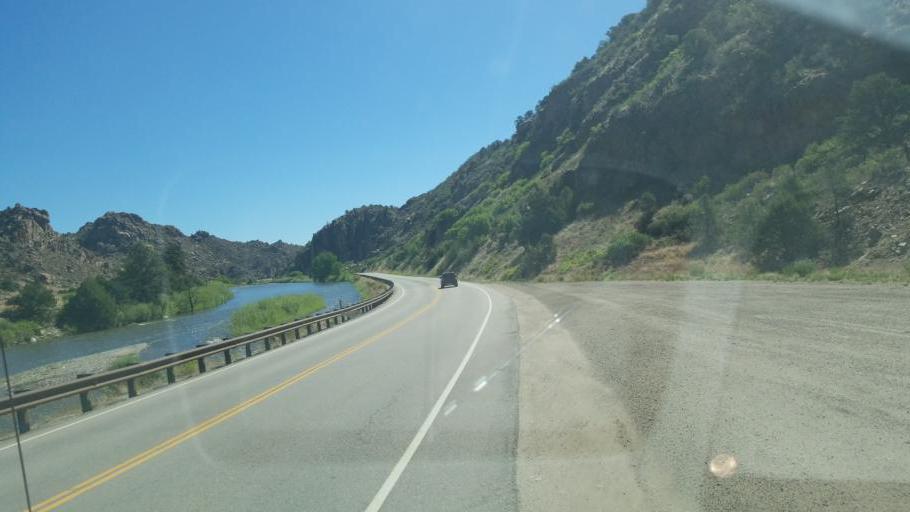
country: US
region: Colorado
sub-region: Custer County
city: Westcliffe
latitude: 38.3904
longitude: -105.6438
